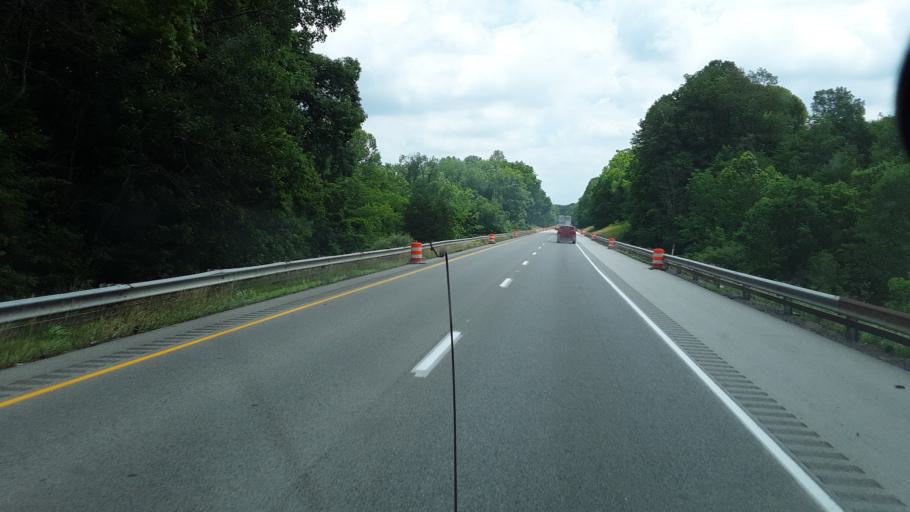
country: US
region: Indiana
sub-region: Putnam County
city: Cloverdale
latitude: 39.5190
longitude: -86.9016
